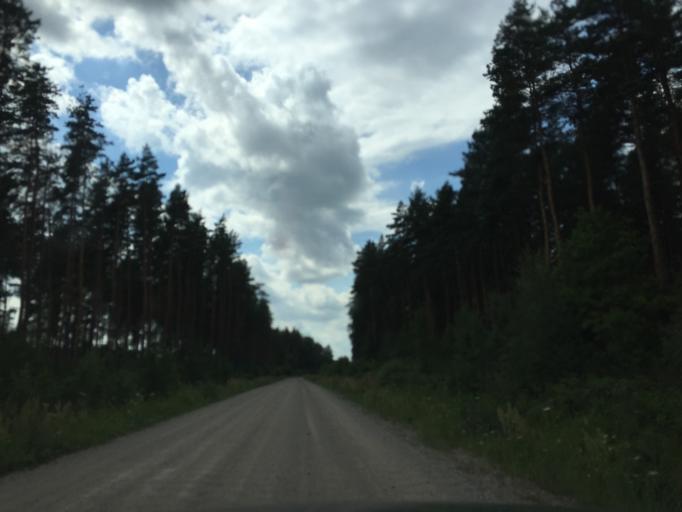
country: LV
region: Jelgava
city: Jelgava
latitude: 56.6250
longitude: 23.6450
